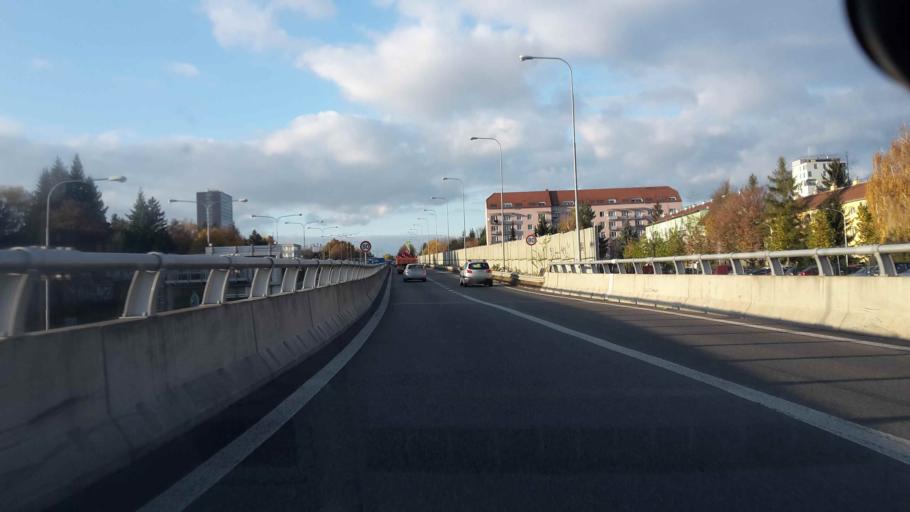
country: CZ
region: South Moravian
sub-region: Mesto Brno
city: Brno
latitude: 49.2182
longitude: 16.5852
